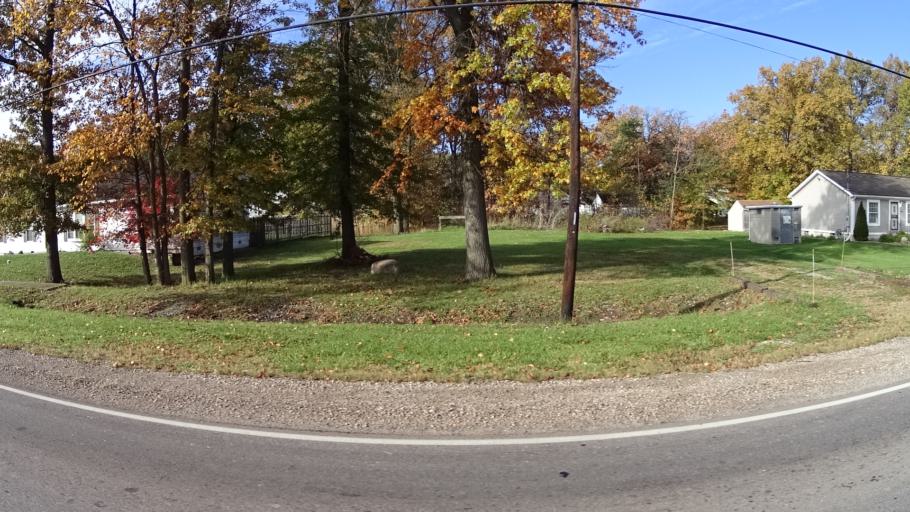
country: US
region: Ohio
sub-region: Lorain County
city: Sheffield
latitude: 41.4308
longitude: -82.1363
